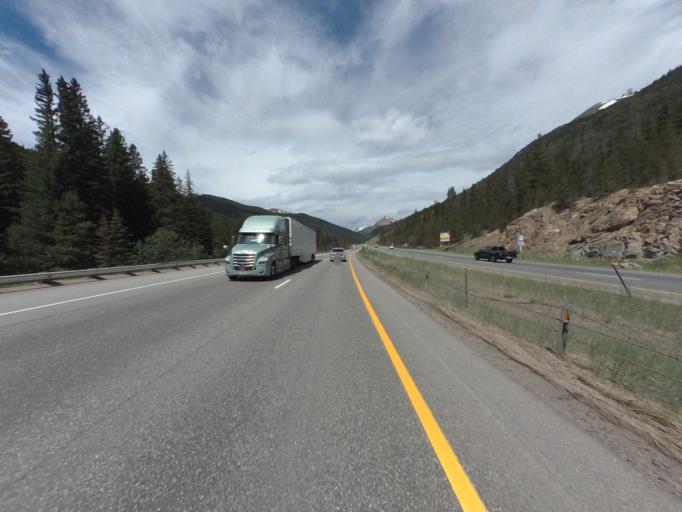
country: US
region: Colorado
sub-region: Clear Creek County
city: Georgetown
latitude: 39.6918
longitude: -105.8110
